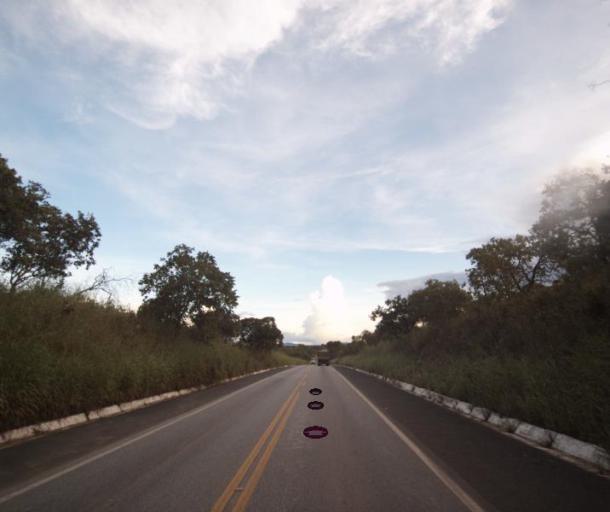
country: BR
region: Goias
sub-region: Uruacu
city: Uruacu
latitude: -14.2221
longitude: -49.1325
